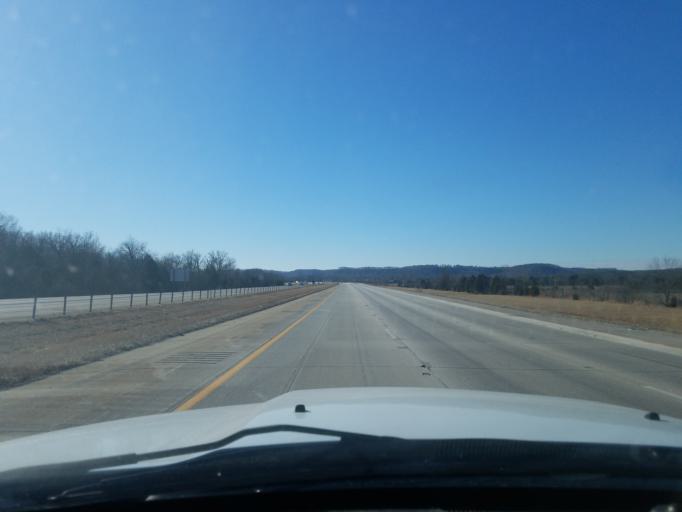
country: US
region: Kentucky
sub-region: Bullitt County
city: Lebanon Junction
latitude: 37.8244
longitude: -85.7254
